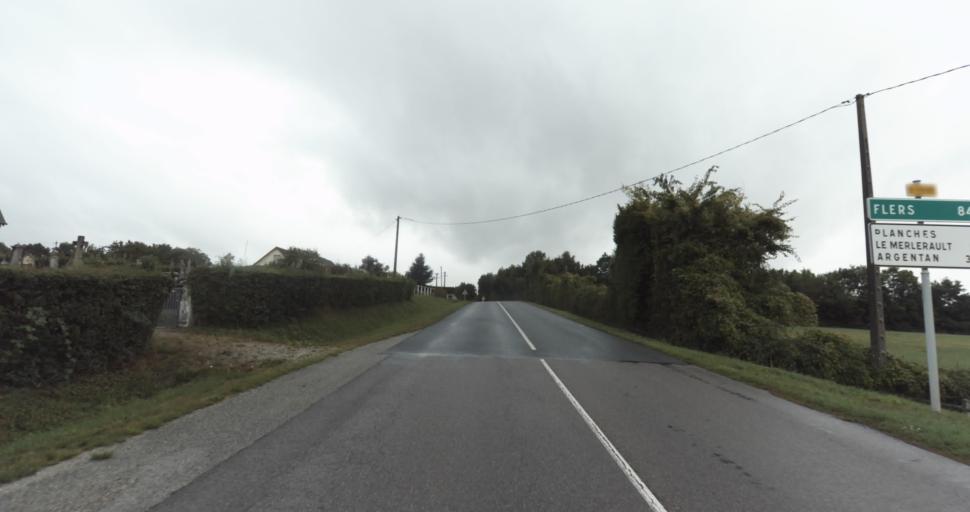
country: FR
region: Lower Normandy
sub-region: Departement de l'Orne
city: Sainte-Gauburge-Sainte-Colombe
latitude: 48.7143
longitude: 0.4254
